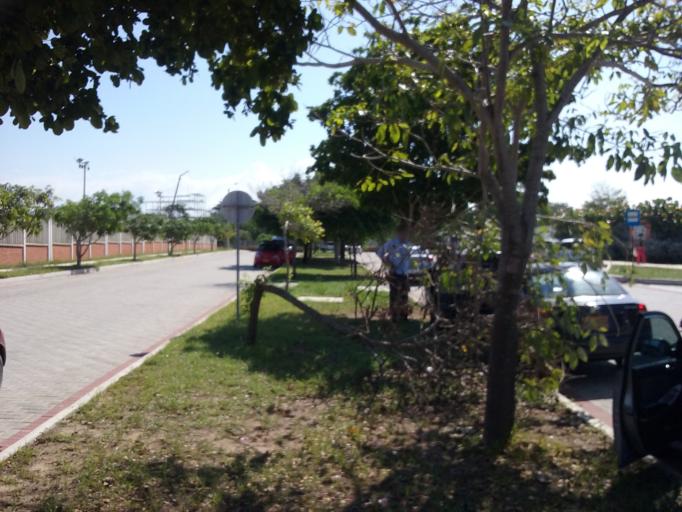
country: CO
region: Atlantico
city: Barranquilla
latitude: 11.0223
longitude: -74.8521
